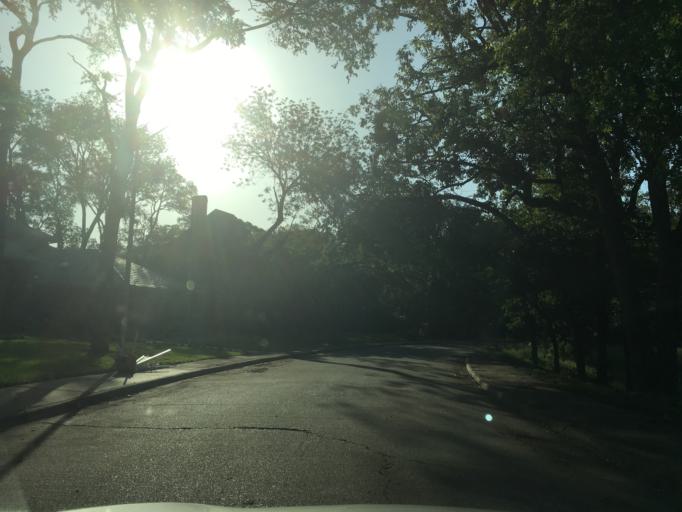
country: US
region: Texas
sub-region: Dallas County
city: Richardson
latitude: 32.8905
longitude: -96.7324
